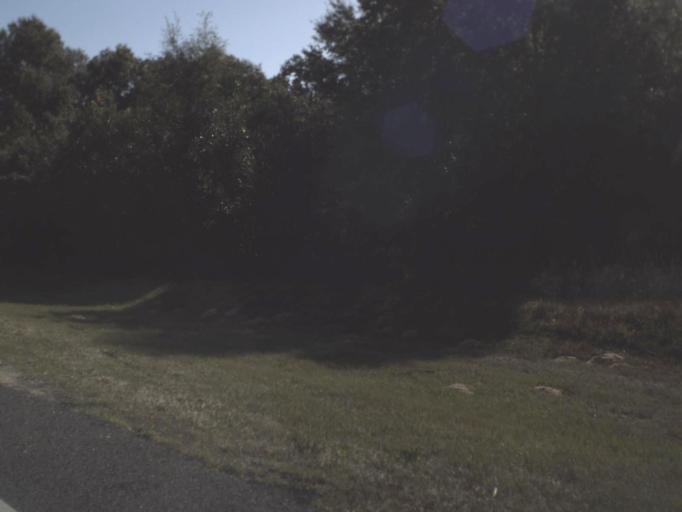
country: US
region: Florida
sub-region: Marion County
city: Belleview
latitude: 29.0292
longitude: -82.0513
